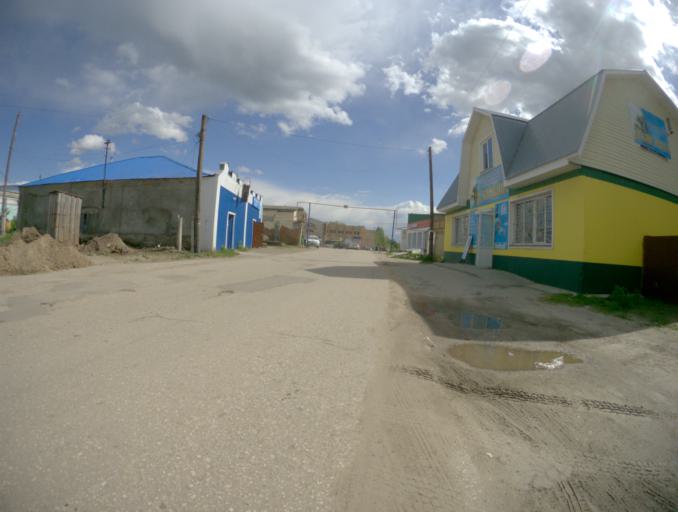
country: RU
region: Rjazan
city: Tuma
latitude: 55.1483
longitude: 40.5554
